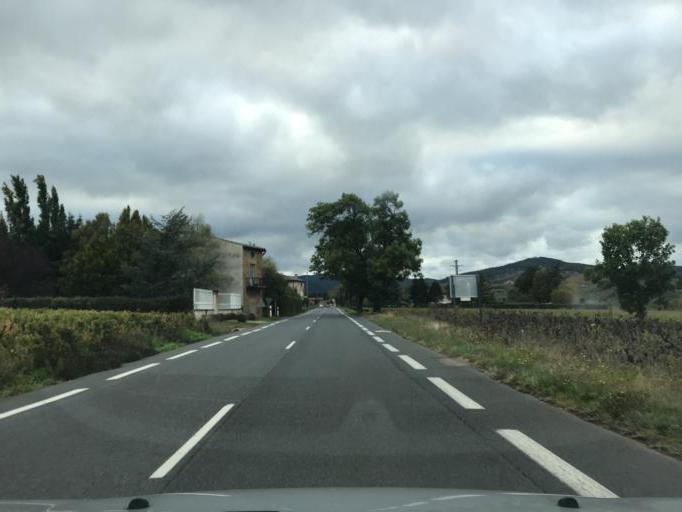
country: FR
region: Rhone-Alpes
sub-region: Departement du Rhone
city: Denice
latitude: 45.9972
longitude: 4.6565
